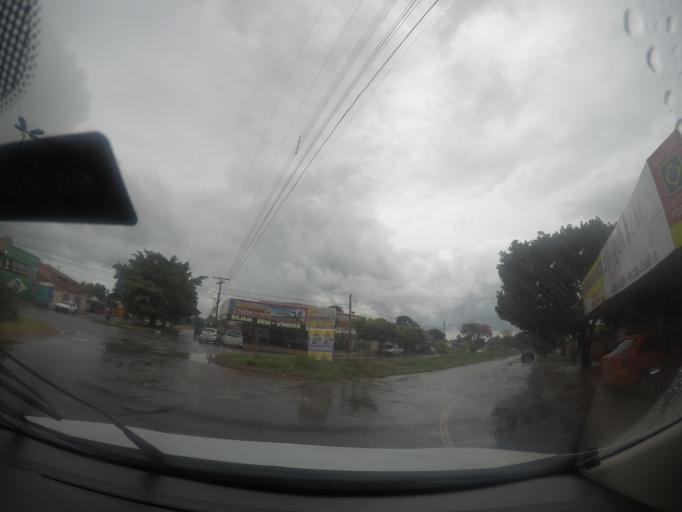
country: BR
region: Goias
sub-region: Trindade
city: Trindade
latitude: -16.6416
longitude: -49.4352
